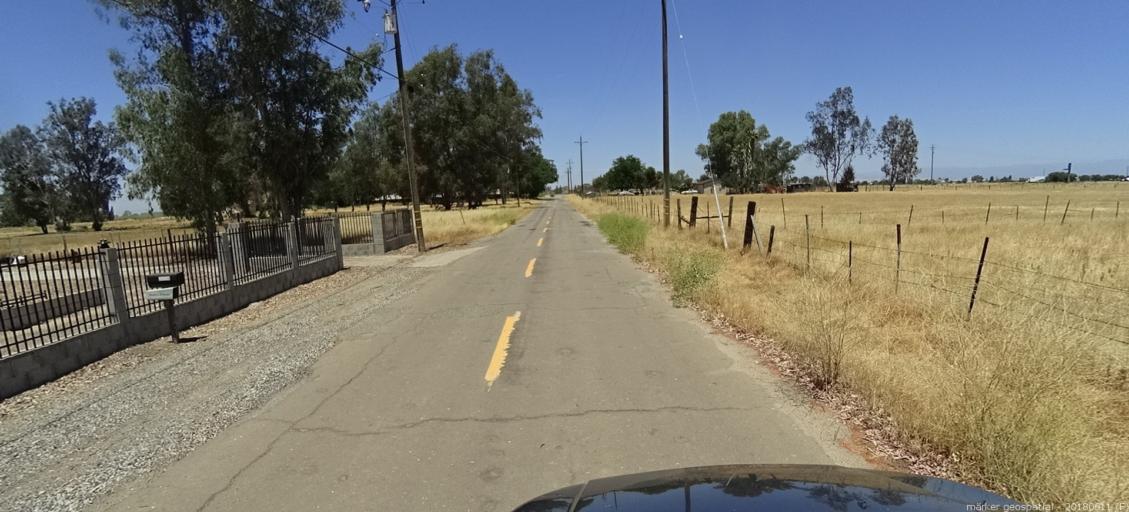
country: US
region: California
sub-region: Madera County
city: Fairmead
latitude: 37.0671
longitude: -120.1934
